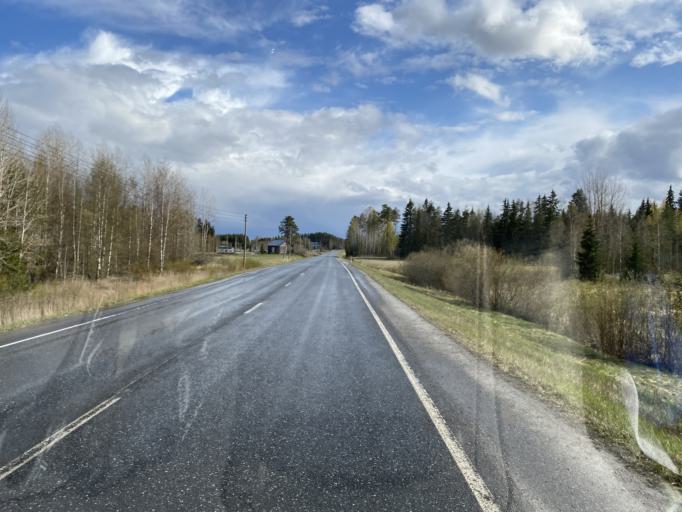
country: FI
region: Pirkanmaa
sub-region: Etelae-Pirkanmaa
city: Viiala
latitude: 61.2127
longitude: 23.7352
